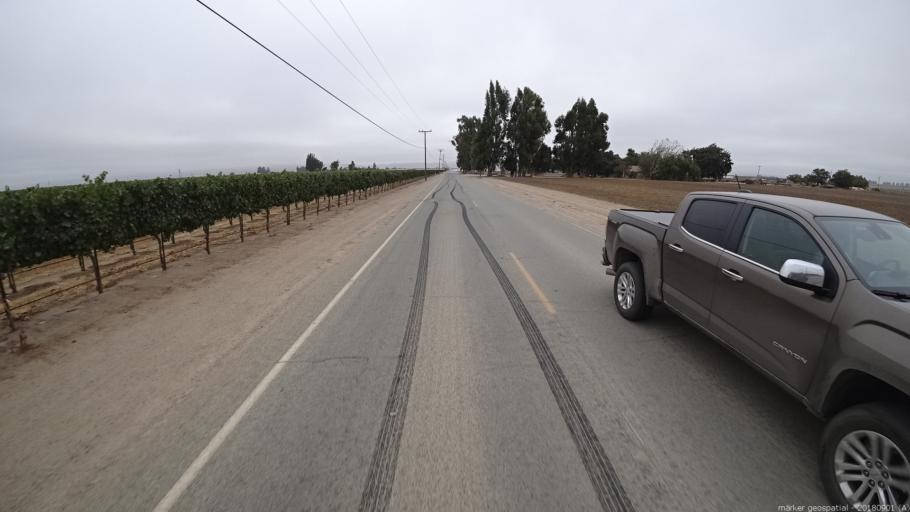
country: US
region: California
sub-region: Monterey County
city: Greenfield
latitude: 36.2961
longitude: -121.2799
